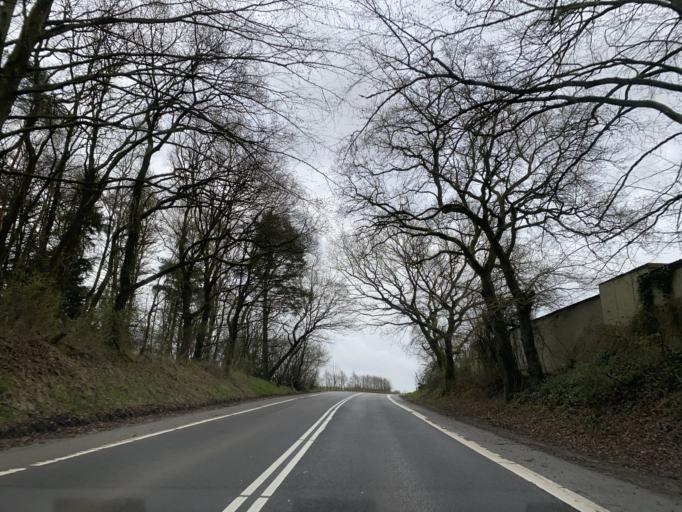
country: DK
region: Central Jutland
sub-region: Viborg Kommune
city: Bjerringbro
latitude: 56.2980
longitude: 9.5998
